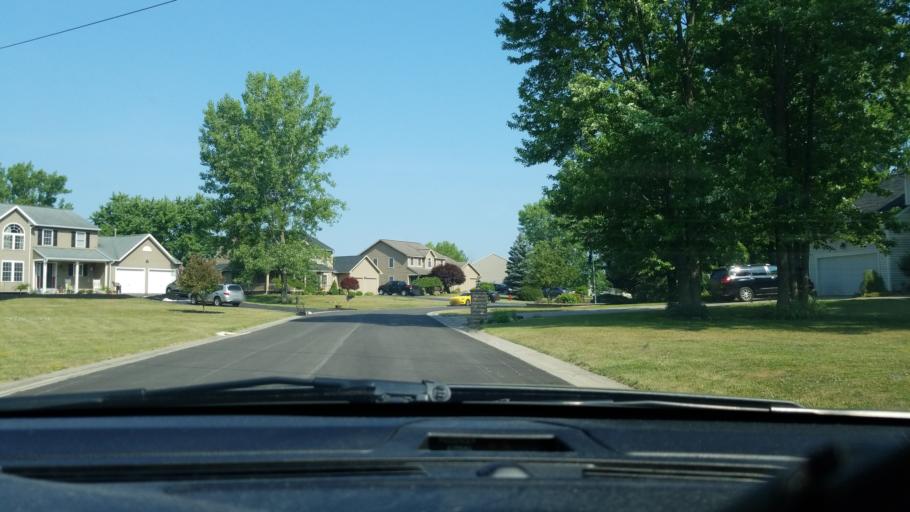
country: US
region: New York
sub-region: Onondaga County
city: East Syracuse
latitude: 43.0966
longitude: -76.0702
